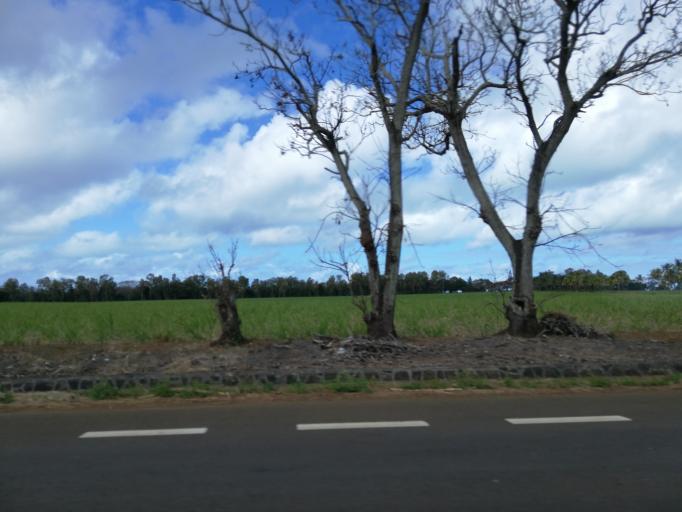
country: MU
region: Grand Port
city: Mahebourg
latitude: -20.3808
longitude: 57.6980
